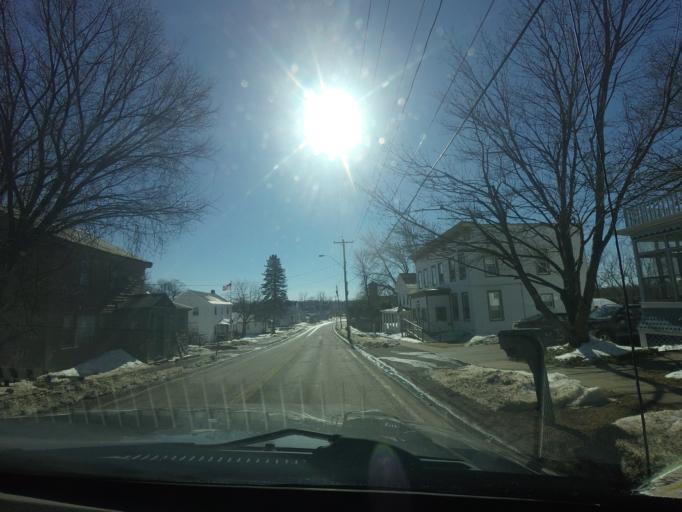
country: US
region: New York
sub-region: Saratoga County
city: Stillwater
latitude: 42.8979
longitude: -73.5862
